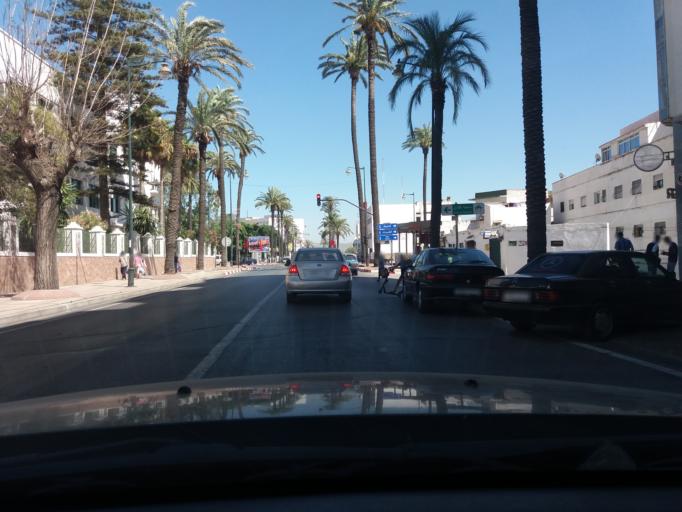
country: MA
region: Tanger-Tetouan
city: Tetouan
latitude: 35.5689
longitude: -5.3809
